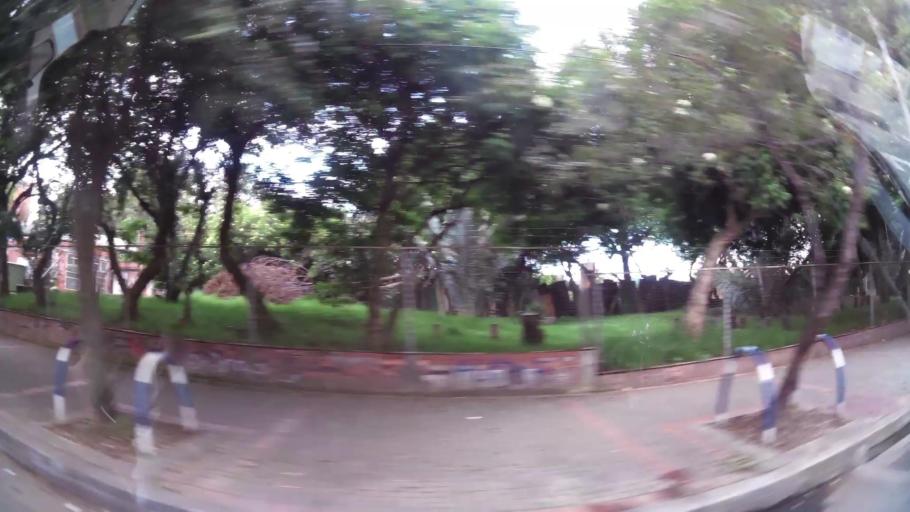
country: CO
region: Cundinamarca
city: Cota
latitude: 4.7300
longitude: -74.0972
